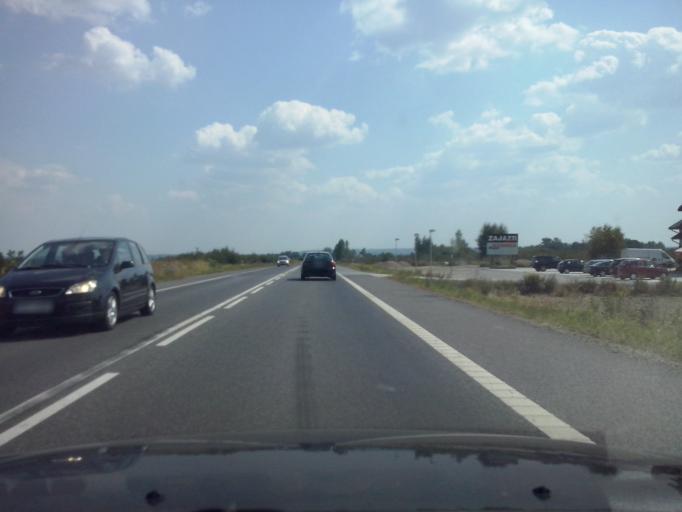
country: PL
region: Swietokrzyskie
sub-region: Powiat sandomierski
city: Loniow
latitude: 50.5549
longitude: 21.5340
